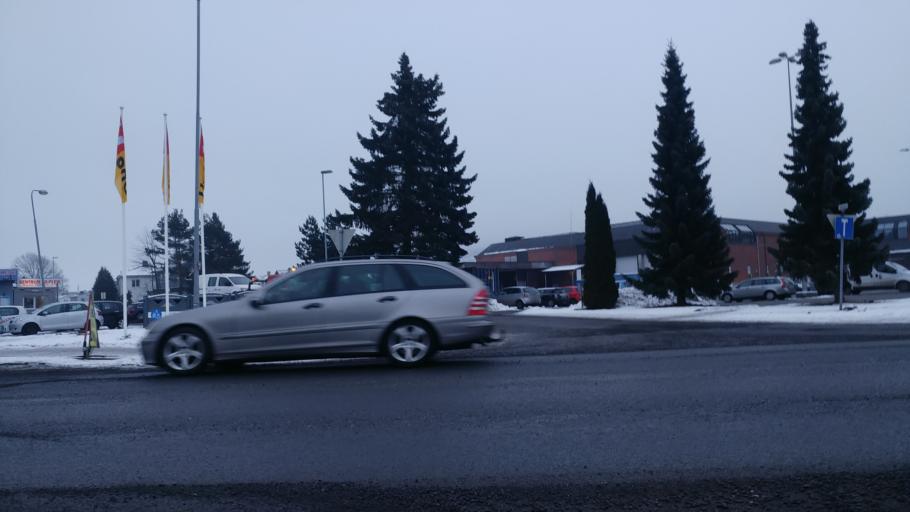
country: NO
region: Akershus
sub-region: Skedsmo
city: Lillestrom
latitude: 59.9581
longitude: 11.0376
